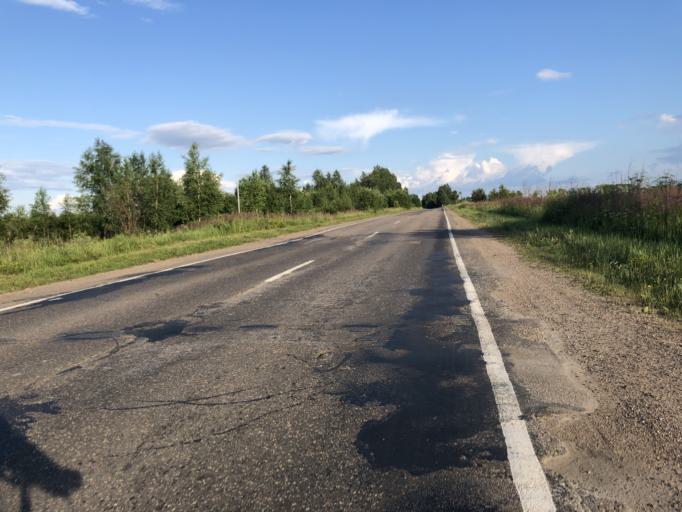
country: RU
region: Tverskaya
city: Rzhev
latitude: 56.2777
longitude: 34.2368
